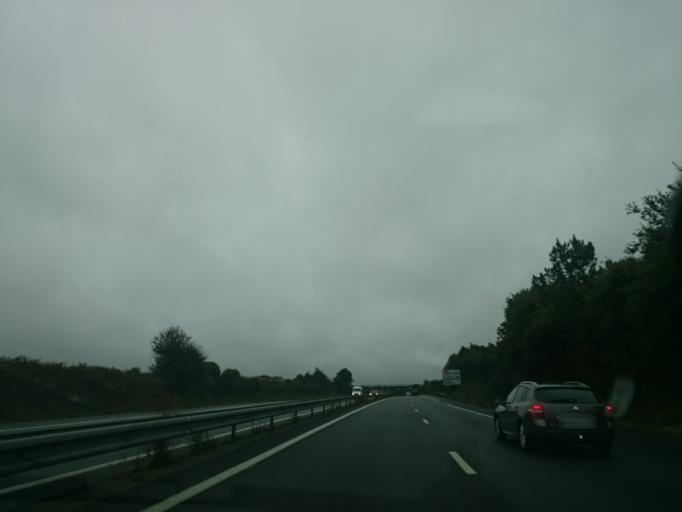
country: FR
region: Brittany
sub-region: Departement du Morbihan
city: Auray
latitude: 47.6766
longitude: -3.0175
